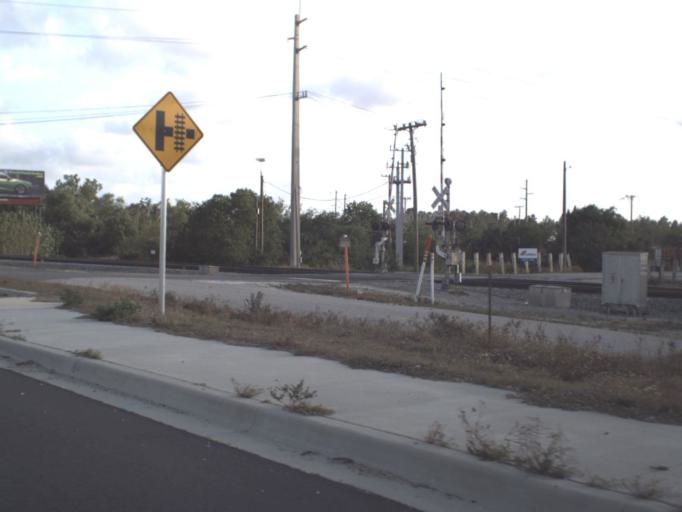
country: US
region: Florida
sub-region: Brevard County
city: Cocoa
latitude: 28.4049
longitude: -80.7552
